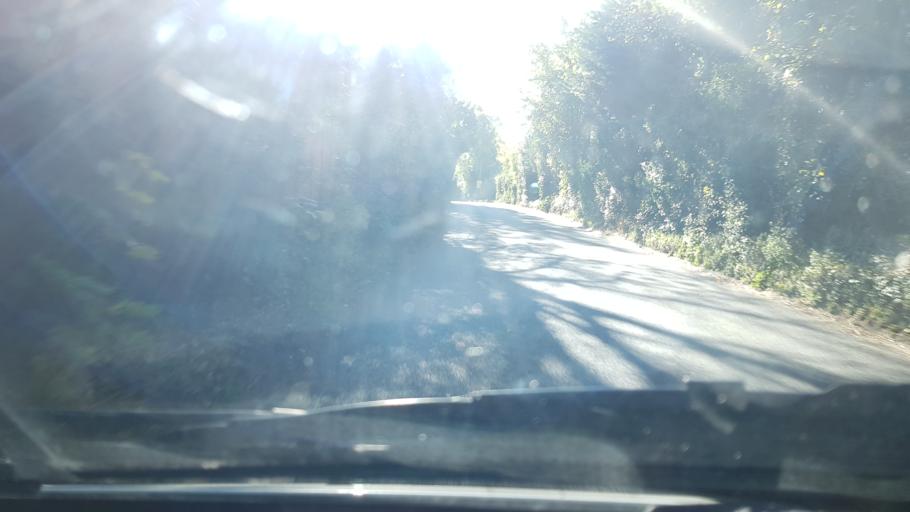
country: GB
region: England
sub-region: Surrey
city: Chilworth
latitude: 51.1905
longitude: -0.5305
